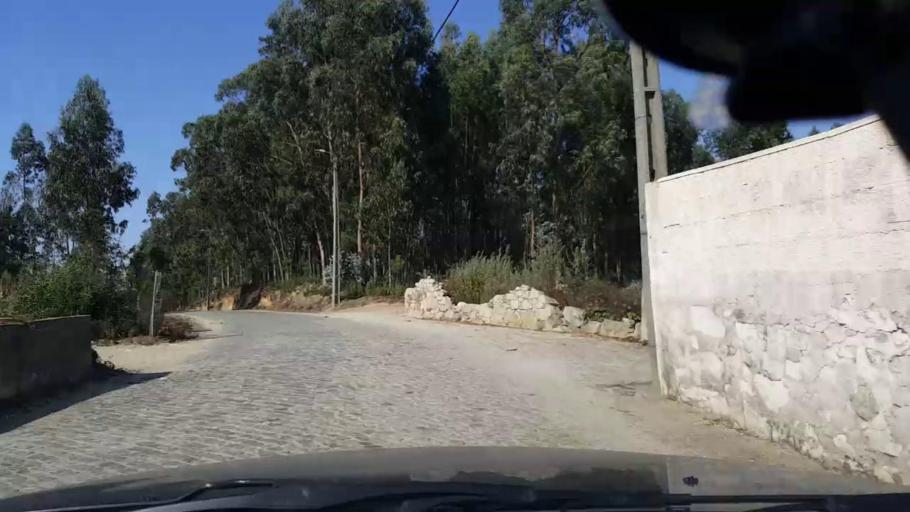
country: PT
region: Porto
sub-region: Vila do Conde
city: Arvore
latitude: 41.3594
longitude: -8.6951
